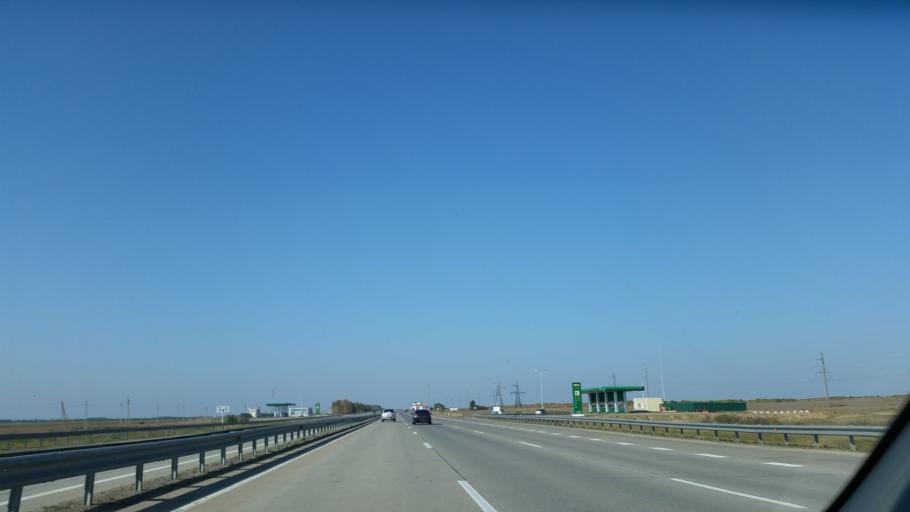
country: KZ
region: Astana Qalasy
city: Astana
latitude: 51.2987
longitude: 71.3565
